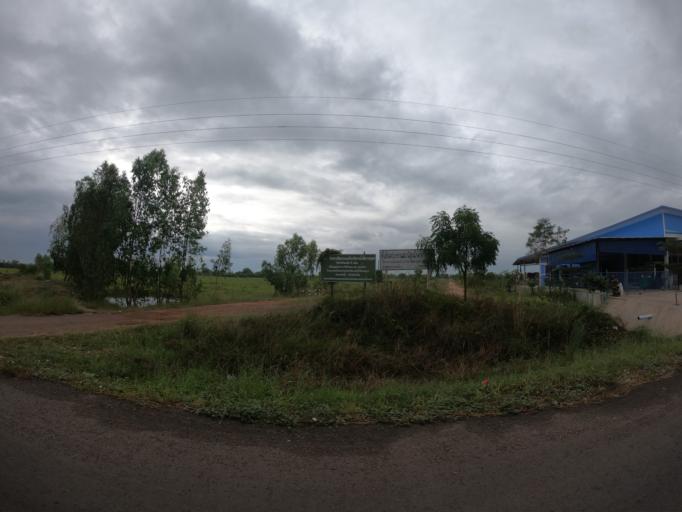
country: TH
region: Roi Et
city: Thawat Buri
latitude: 16.0942
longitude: 103.7860
